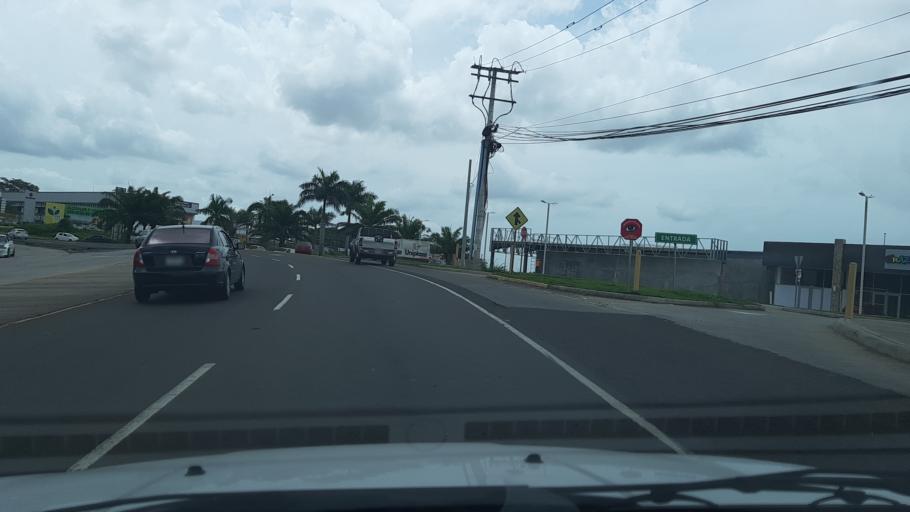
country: PA
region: Panama
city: La Chorrera
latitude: 8.8982
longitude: -79.7554
